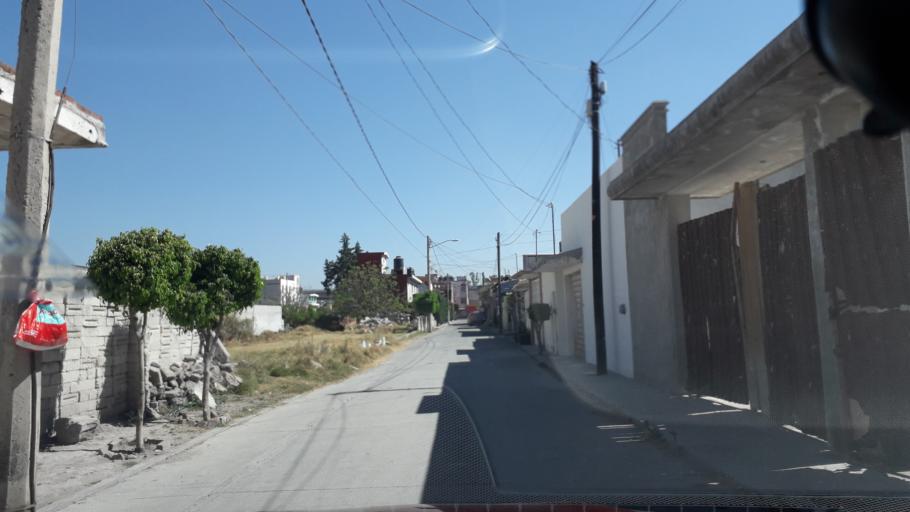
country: MX
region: Puebla
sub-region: Cuautlancingo
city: Sanctorum
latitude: 19.0861
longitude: -98.2182
